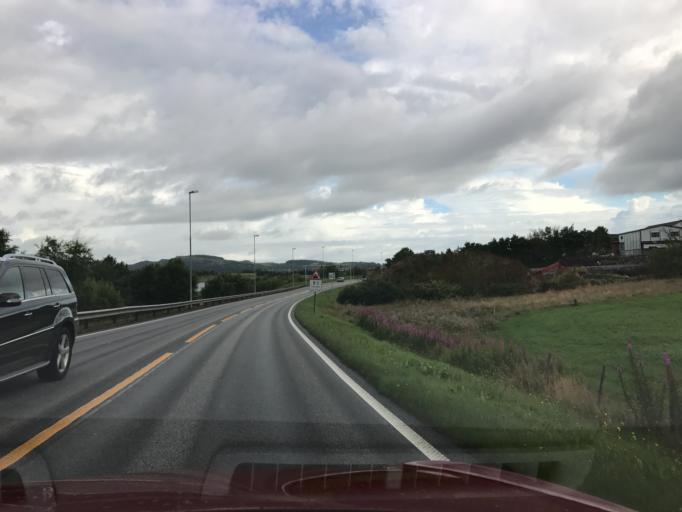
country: NO
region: Rogaland
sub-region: Rennesoy
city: Vikevag
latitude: 59.0681
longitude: 5.6731
